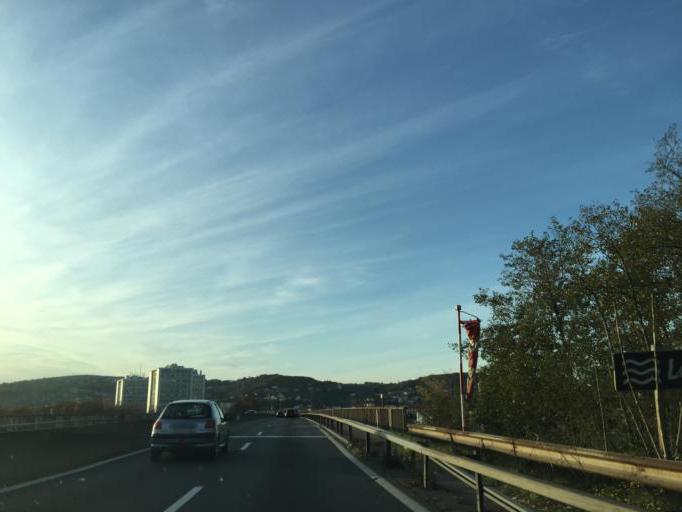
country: FR
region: Rhone-Alpes
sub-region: Departement du Rhone
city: Givors
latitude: 45.5889
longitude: 4.7796
